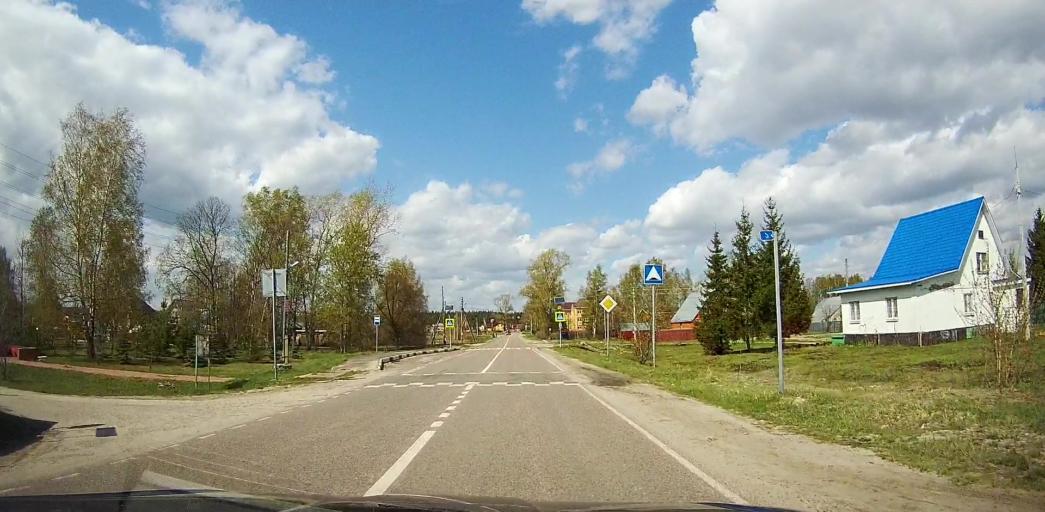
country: RU
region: Moskovskaya
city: Davydovo
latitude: 55.5560
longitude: 38.8146
